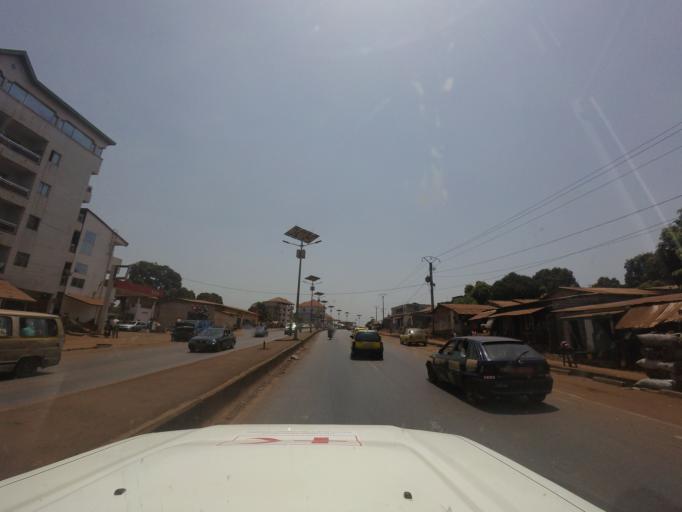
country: GN
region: Kindia
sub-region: Prefecture de Dubreka
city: Dubreka
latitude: 9.6517
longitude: -13.5485
